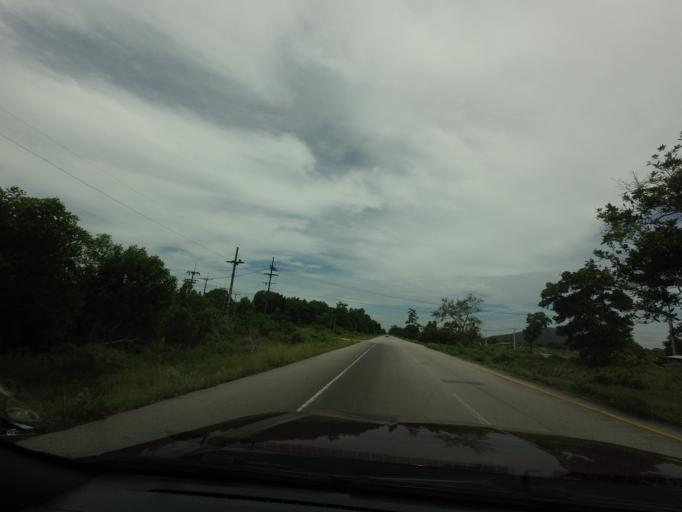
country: TH
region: Narathiwat
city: Narathiwat
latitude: 6.3562
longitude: 101.9038
